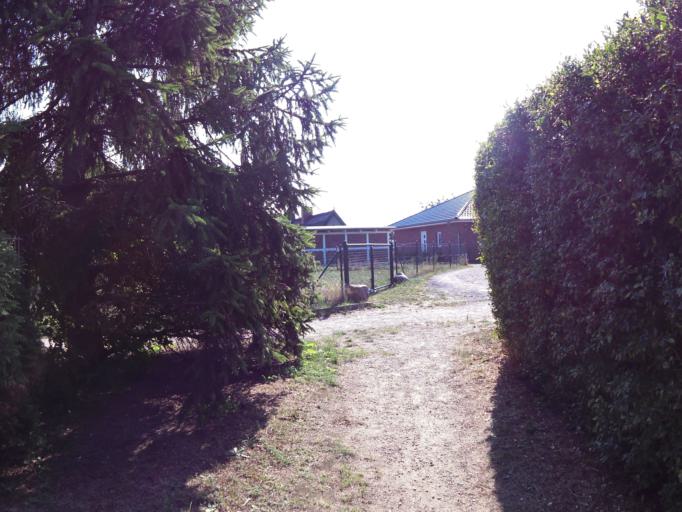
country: DE
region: Mecklenburg-Vorpommern
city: Loddin
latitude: 54.0134
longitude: 14.0453
